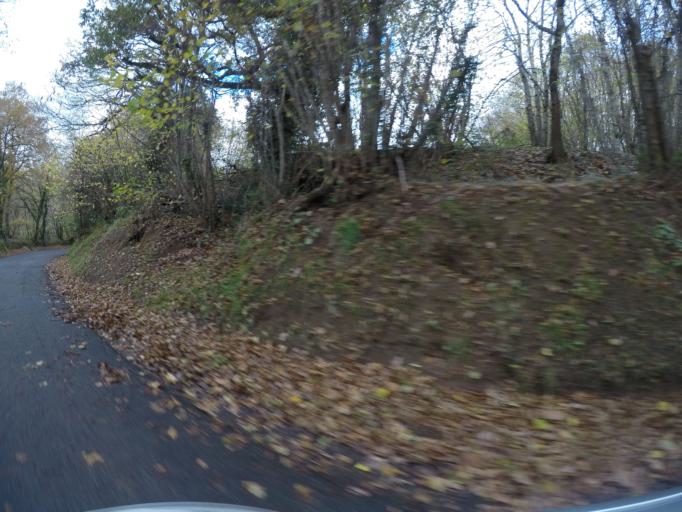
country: FR
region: Brittany
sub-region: Departement des Cotes-d'Armor
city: Graces
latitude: 48.5262
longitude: -3.1814
